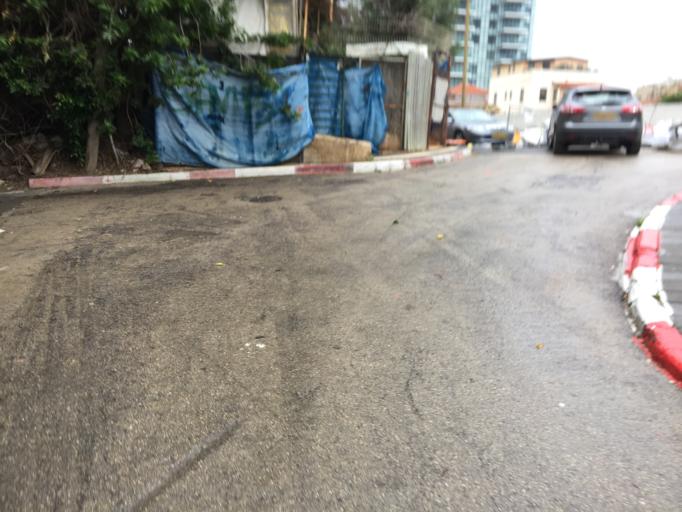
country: IL
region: Tel Aviv
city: Yafo
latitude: 32.0606
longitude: 34.7665
